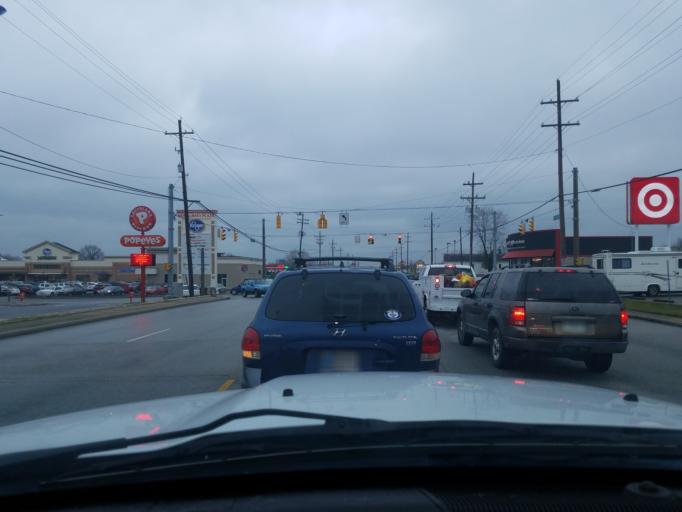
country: US
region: Indiana
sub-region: Floyd County
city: New Albany
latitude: 38.3059
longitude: -85.8406
